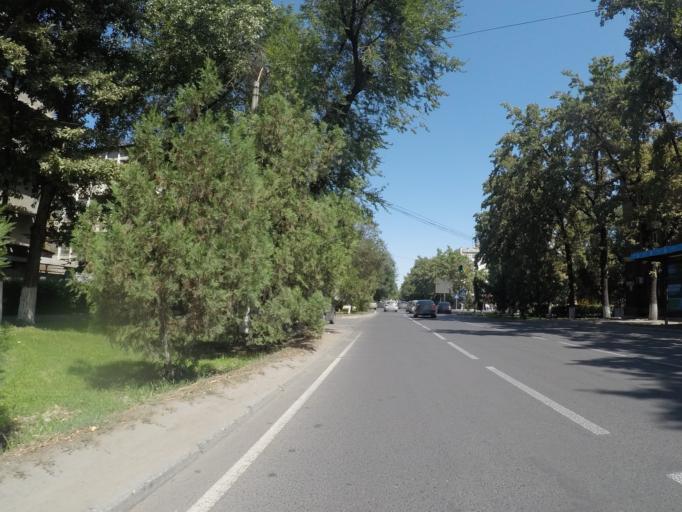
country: KG
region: Chuy
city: Bishkek
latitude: 42.8806
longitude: 74.5963
